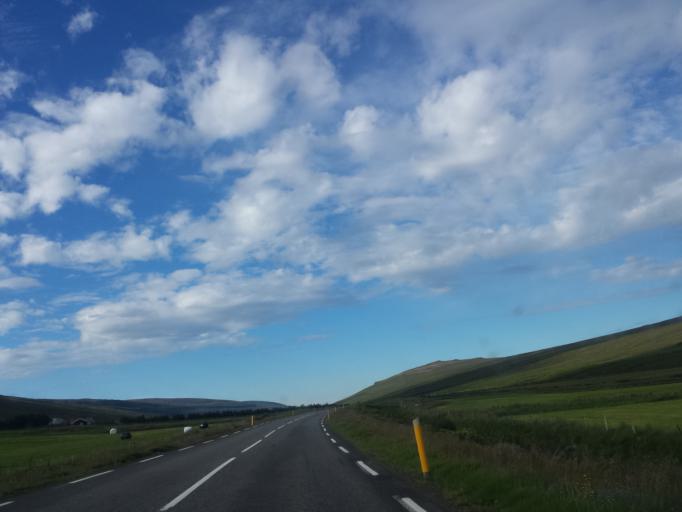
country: IS
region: Northeast
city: Laugar
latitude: 65.7440
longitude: -17.5915
